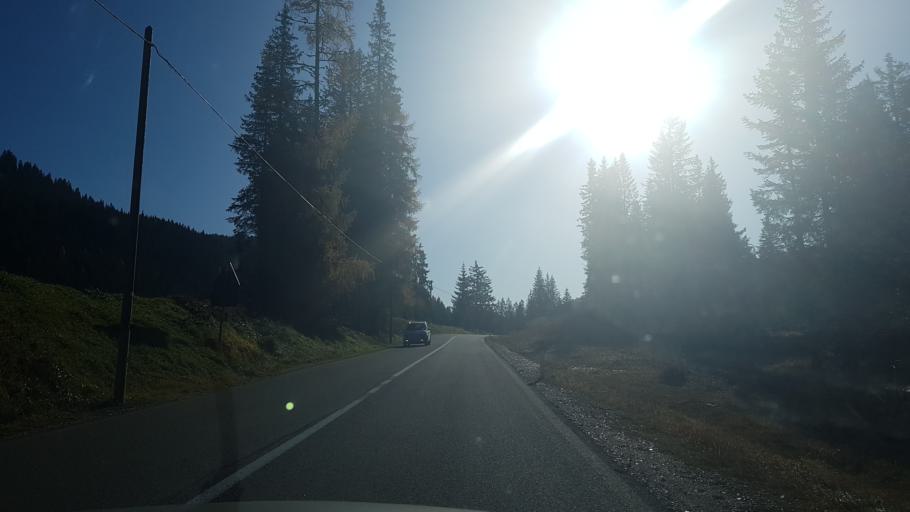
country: IT
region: Trentino-Alto Adige
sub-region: Bolzano
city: Sesto
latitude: 46.6689
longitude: 12.3974
